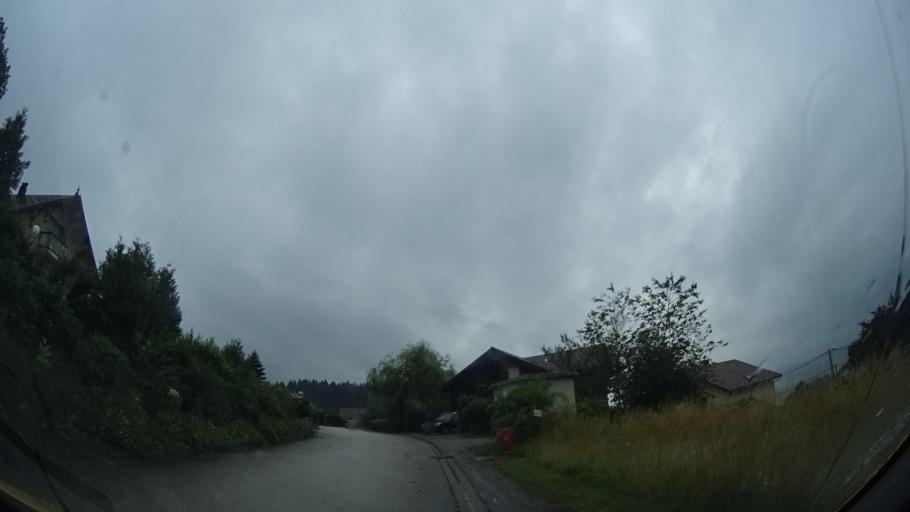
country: FR
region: Franche-Comte
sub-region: Departement du Doubs
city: Les Fourgs
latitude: 46.8278
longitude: 6.3429
